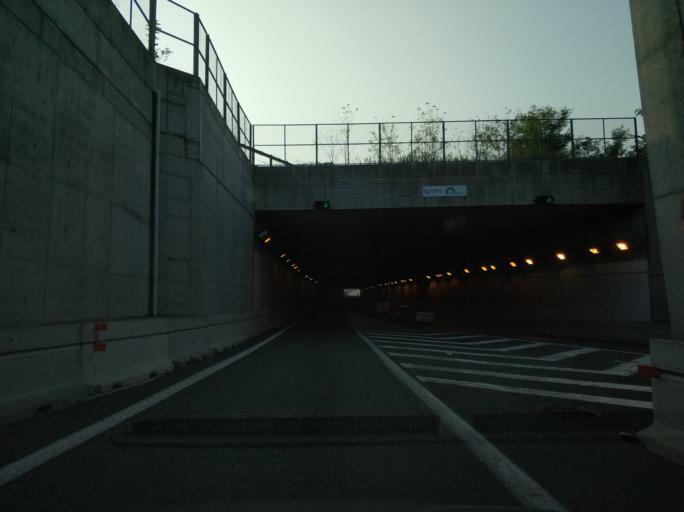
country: IT
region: Piedmont
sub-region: Provincia di Torino
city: Borgaro Torinese
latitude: 45.1454
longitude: 7.6497
